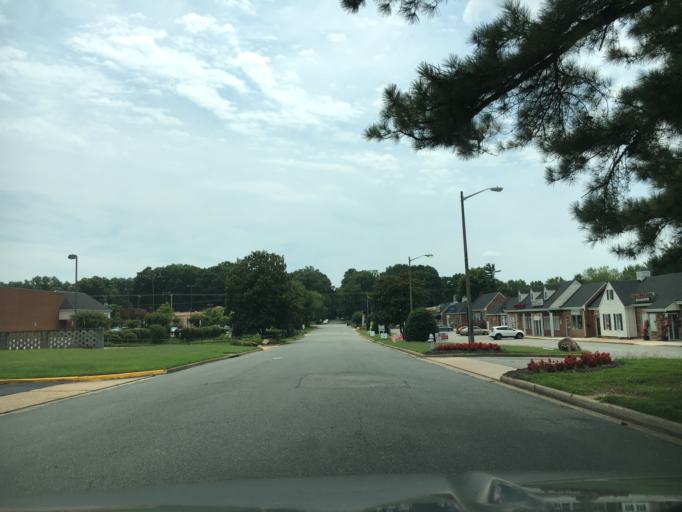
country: US
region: Virginia
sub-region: Henrico County
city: Short Pump
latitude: 37.6000
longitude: -77.6229
